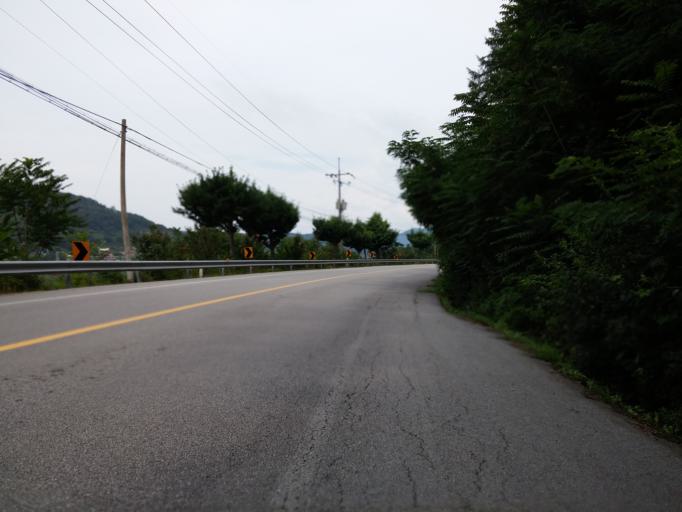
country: KR
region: Chungcheongnam-do
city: Gongju
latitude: 36.4441
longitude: 127.1870
